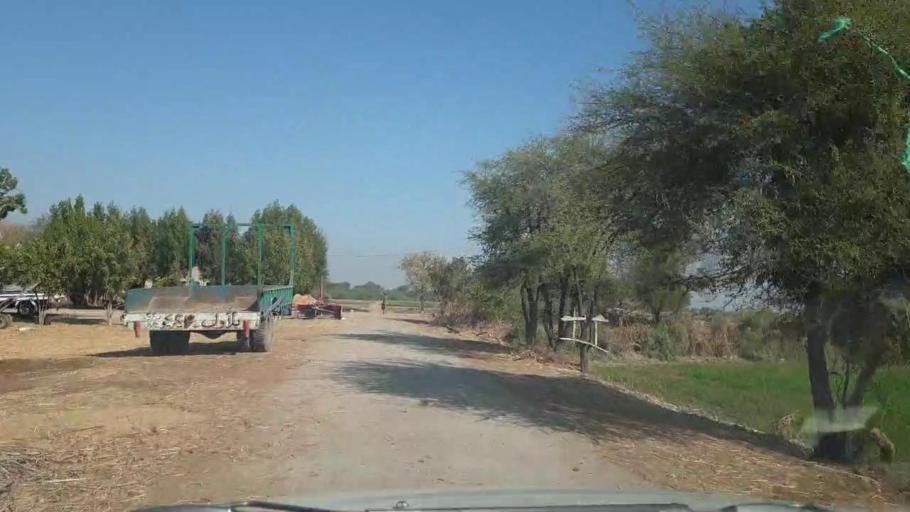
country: PK
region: Sindh
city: Mirpur Khas
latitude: 25.5099
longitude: 69.1370
